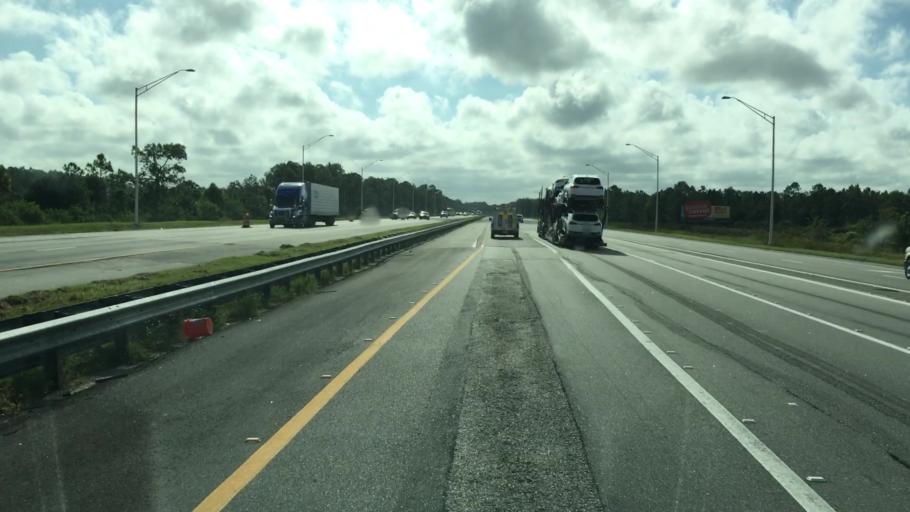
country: US
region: Florida
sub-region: Volusia County
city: South Daytona
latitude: 29.1464
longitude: -81.0707
